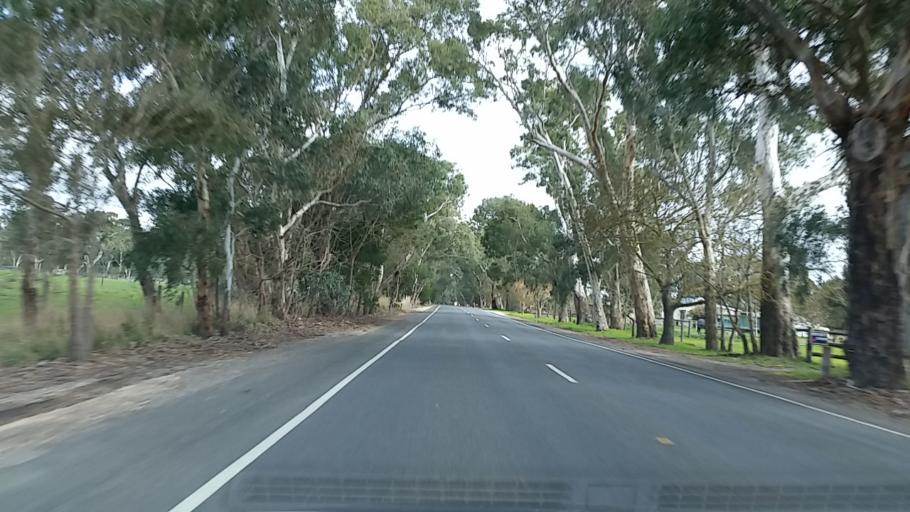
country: AU
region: South Australia
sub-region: Mount Barker
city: Meadows
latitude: -35.1957
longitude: 138.7253
